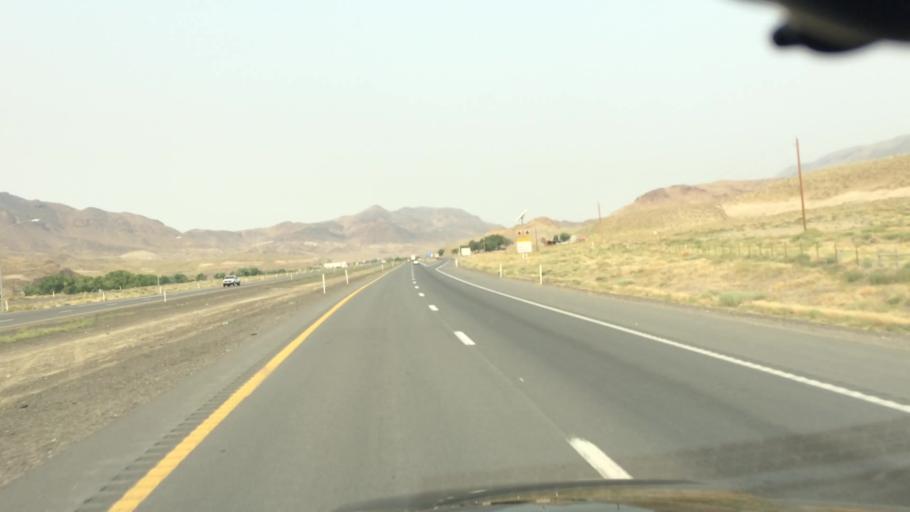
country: US
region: Nevada
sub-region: Lyon County
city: Fernley
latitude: 39.6054
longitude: -119.3280
